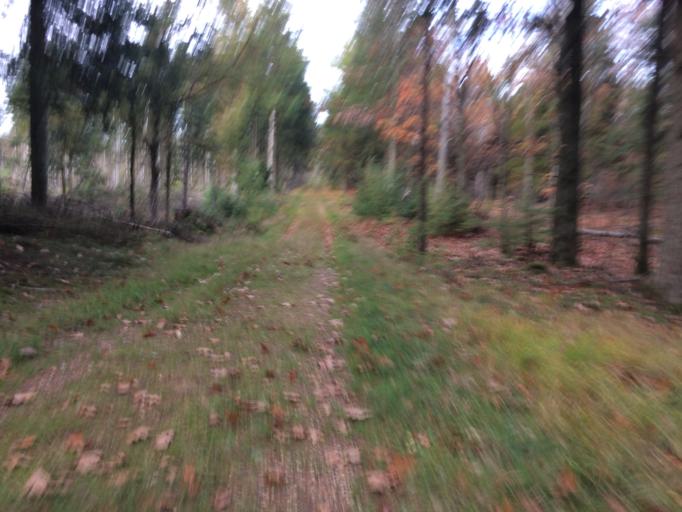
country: DK
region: Central Jutland
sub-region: Holstebro Kommune
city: Ulfborg
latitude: 56.2123
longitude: 8.4442
